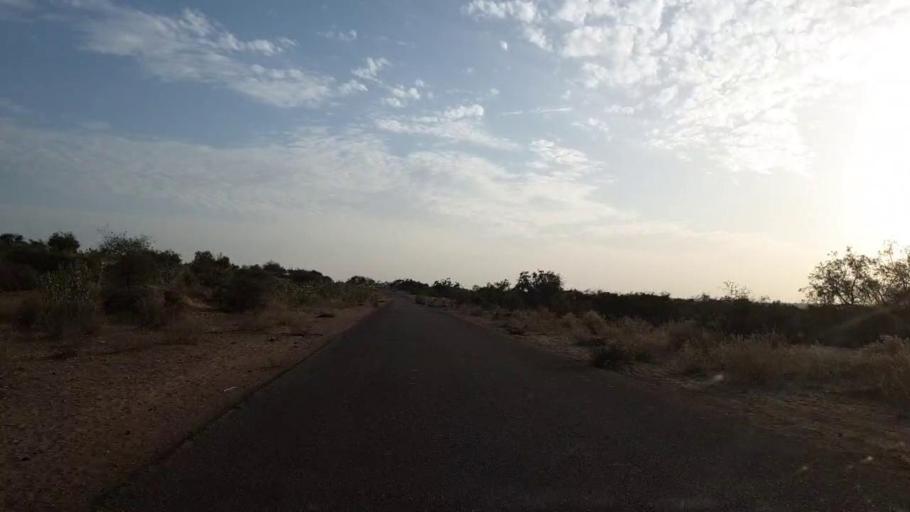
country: PK
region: Sindh
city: Nabisar
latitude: 25.1038
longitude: 69.9944
